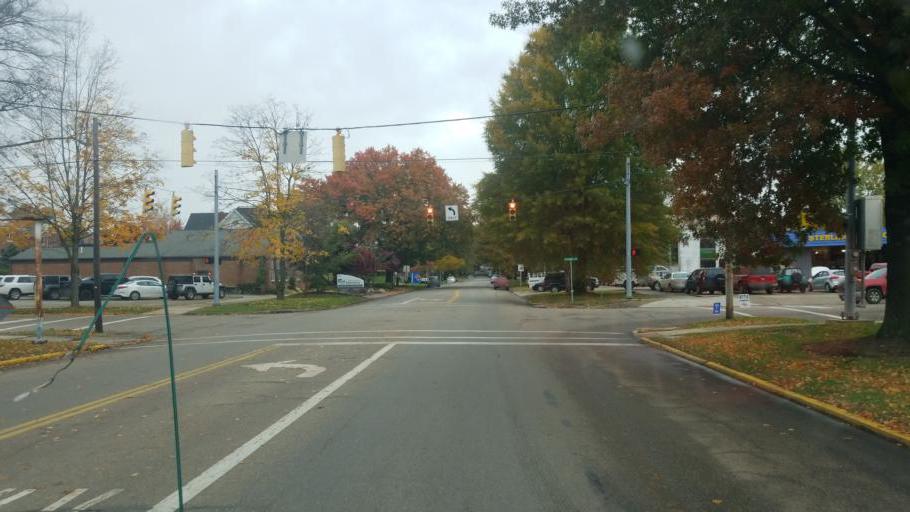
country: US
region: Ohio
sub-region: Washington County
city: Marietta
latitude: 39.4171
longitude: -81.4564
